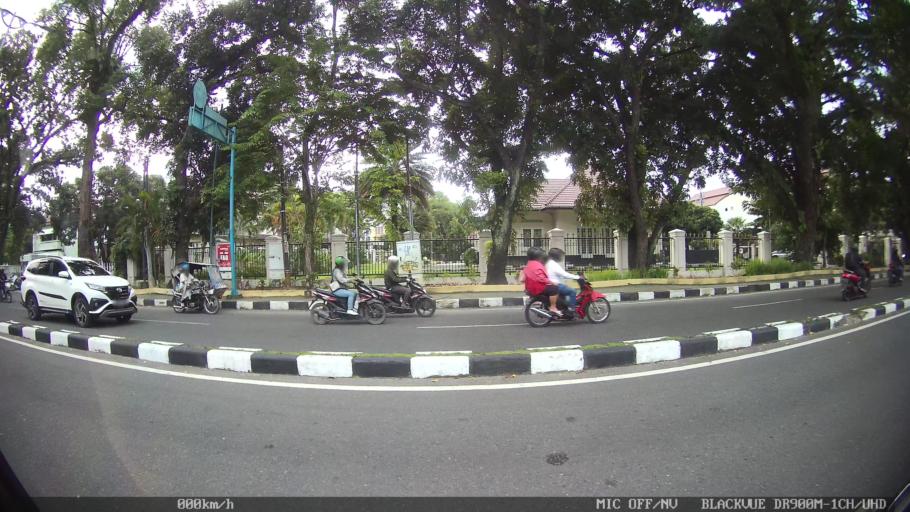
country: ID
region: North Sumatra
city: Medan
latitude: 3.5793
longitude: 98.6791
